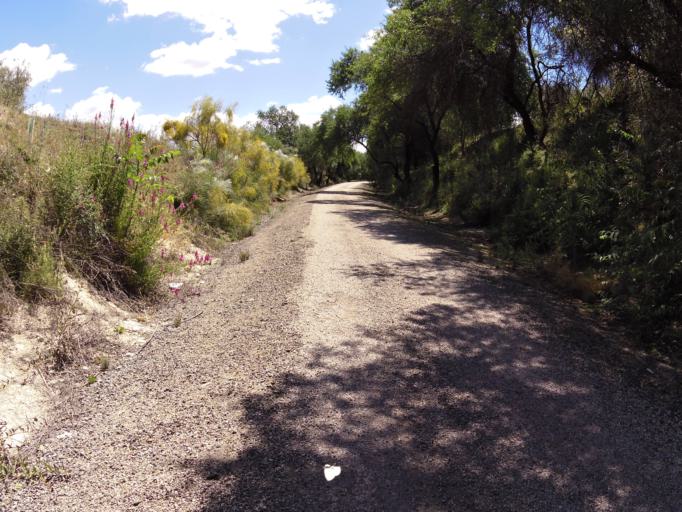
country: ES
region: Andalusia
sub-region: Provincia de Jaen
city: Alcaudete
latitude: 37.6649
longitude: -4.0524
